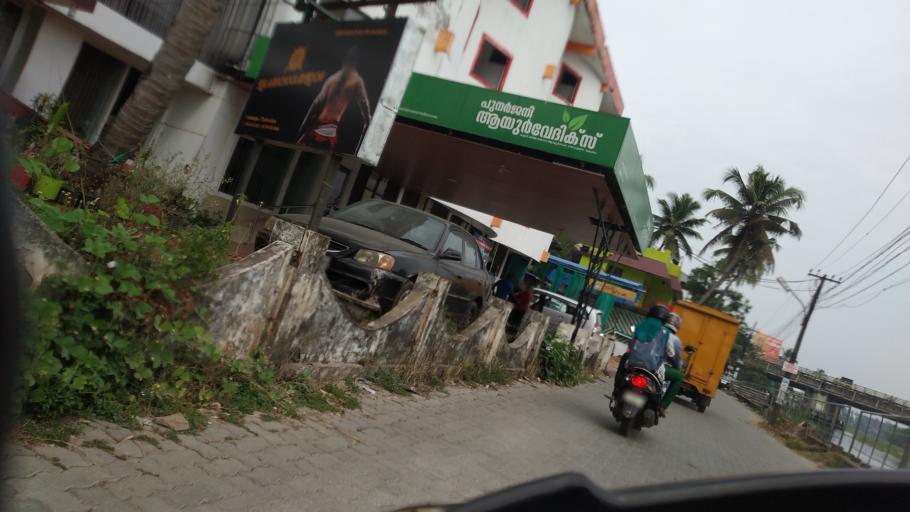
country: IN
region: Kerala
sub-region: Ernakulam
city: Cochin
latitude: 9.9546
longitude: 76.3165
